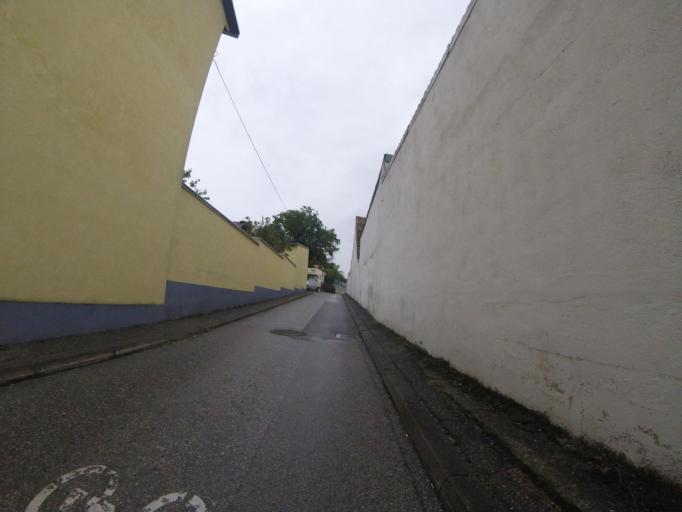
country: AT
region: Burgenland
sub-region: Eisenstadt-Umgebung
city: Donnerskirchen
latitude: 47.8984
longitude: 16.6425
